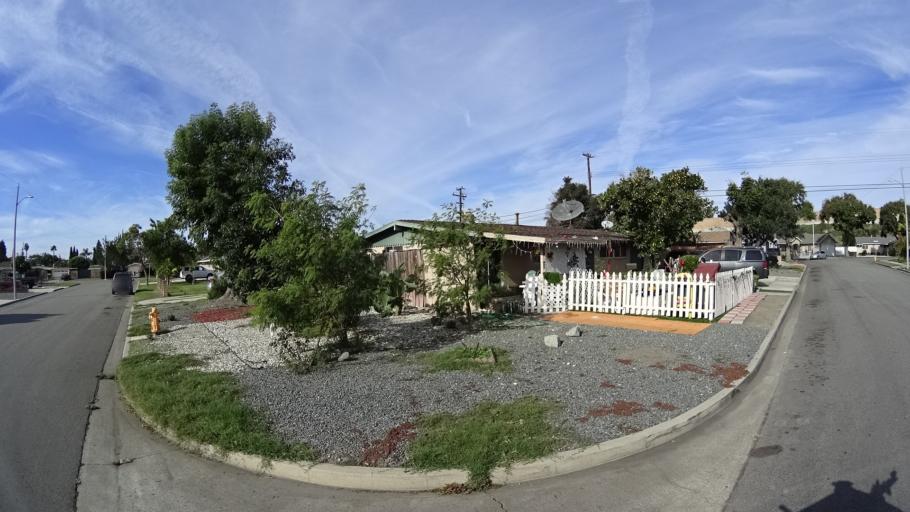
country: US
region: California
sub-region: Orange County
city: Garden Grove
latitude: 33.7646
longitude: -117.9311
